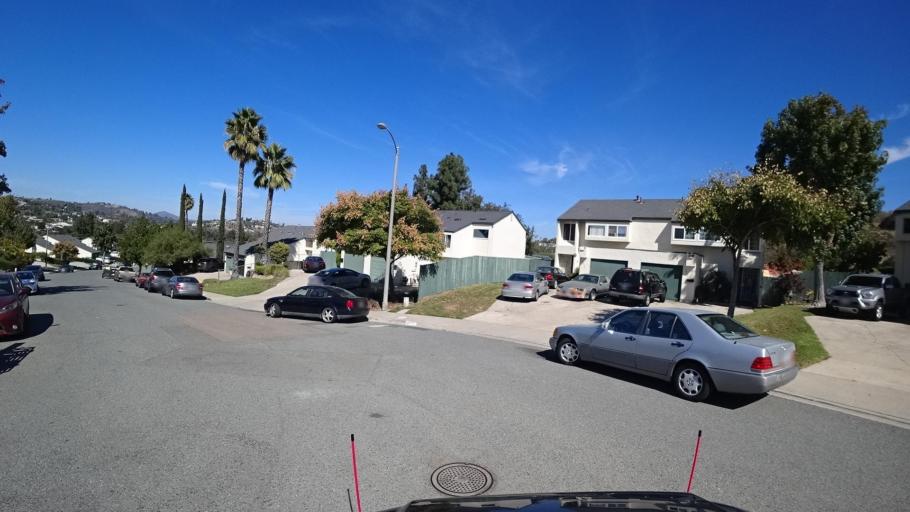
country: US
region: California
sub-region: San Diego County
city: La Presa
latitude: 32.7258
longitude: -117.0093
